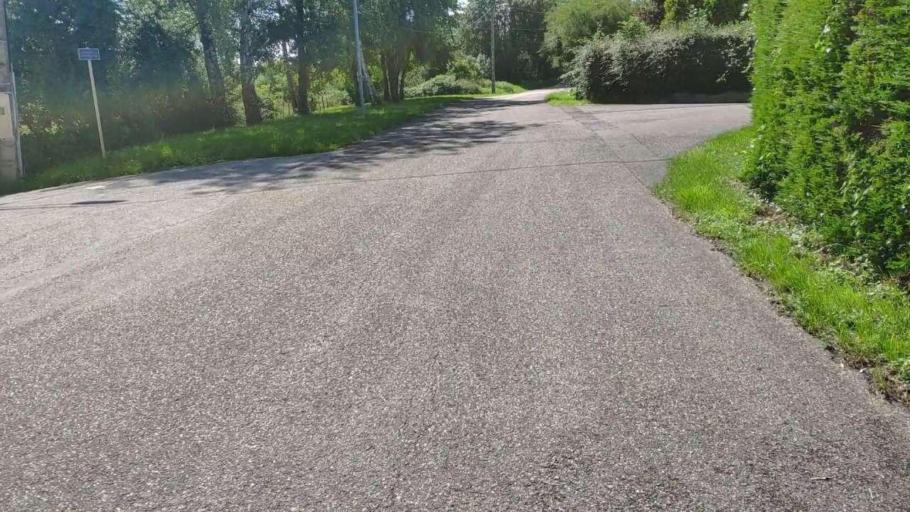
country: FR
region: Franche-Comte
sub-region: Departement du Jura
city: Bletterans
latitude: 46.8249
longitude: 5.5557
